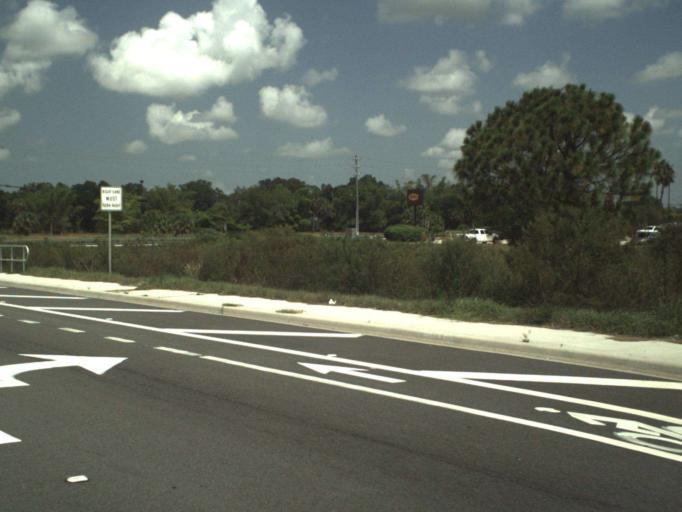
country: US
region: Florida
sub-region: Saint Lucie County
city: Lakewood Park
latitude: 27.4476
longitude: -80.3977
